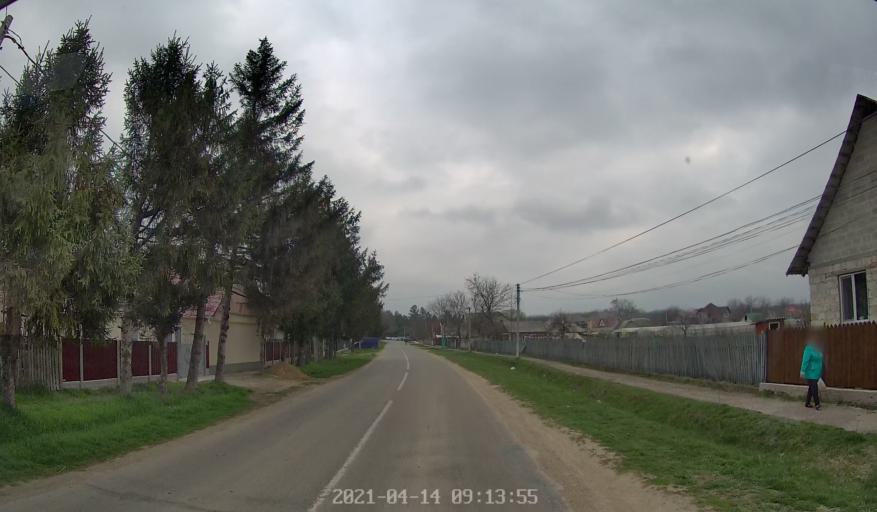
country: MD
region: Chisinau
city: Vadul lui Voda
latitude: 47.1052
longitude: 29.1138
